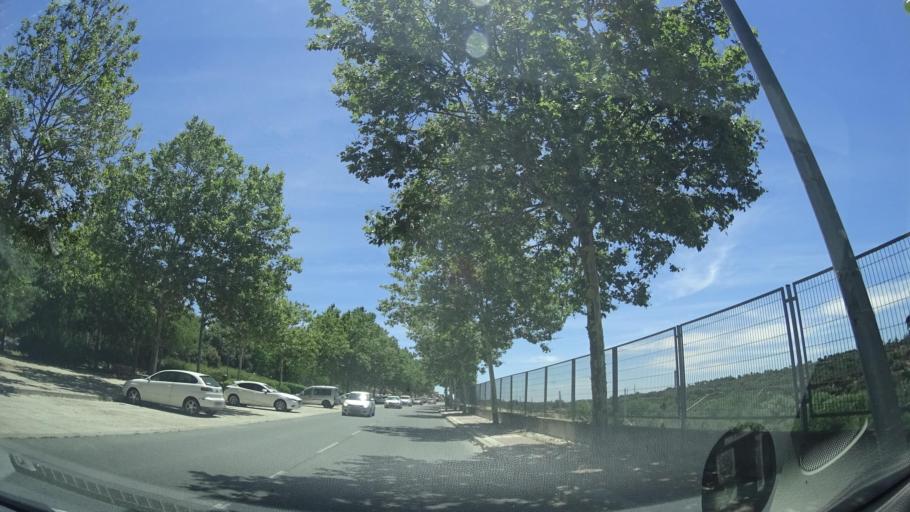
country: ES
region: Madrid
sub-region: Provincia de Madrid
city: Collado-Villalba
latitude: 40.6242
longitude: -3.9994
